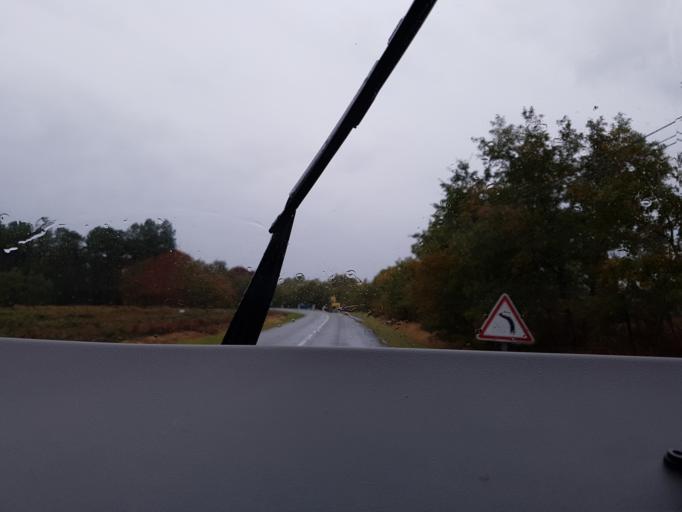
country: FR
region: Aquitaine
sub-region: Departement des Landes
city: Pissos
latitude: 44.3627
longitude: -0.6384
